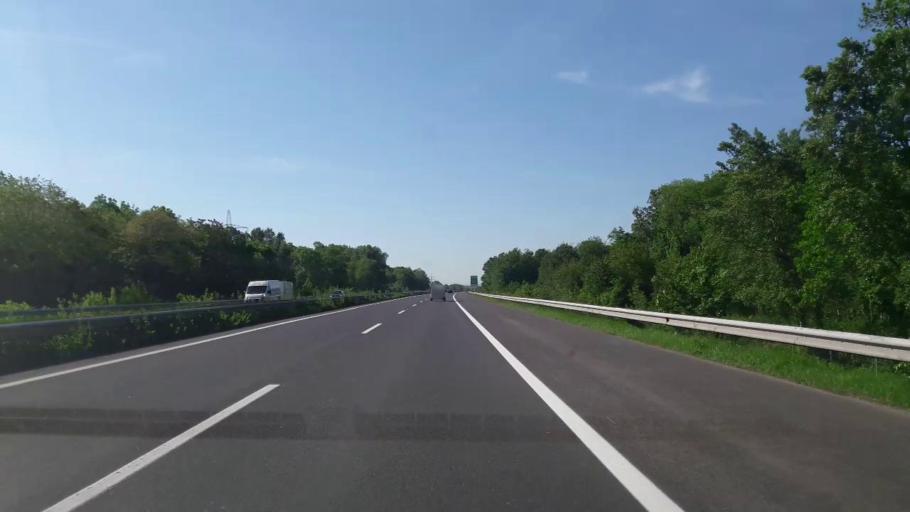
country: AT
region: Burgenland
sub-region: Eisenstadt-Umgebung
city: Wimpassing an der Leitha
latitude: 47.9015
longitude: 16.4133
